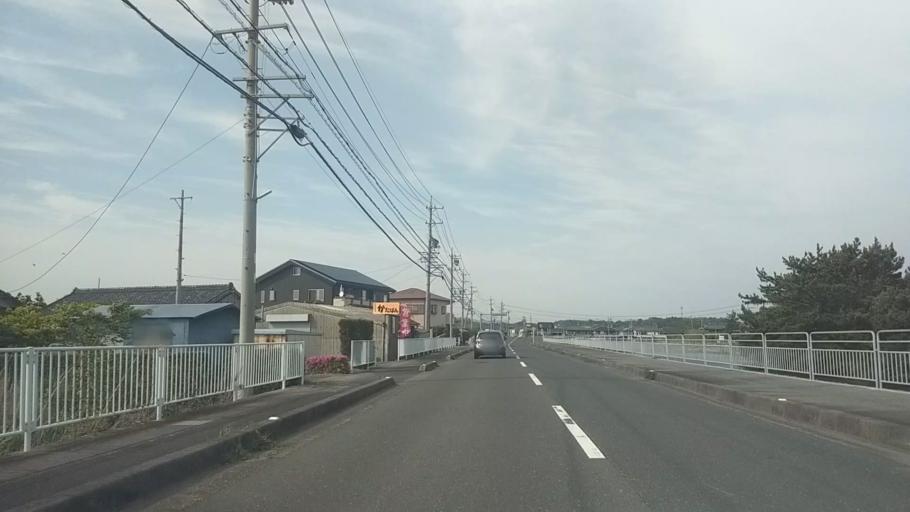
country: JP
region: Shizuoka
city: Kosai-shi
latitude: 34.7192
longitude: 137.5922
